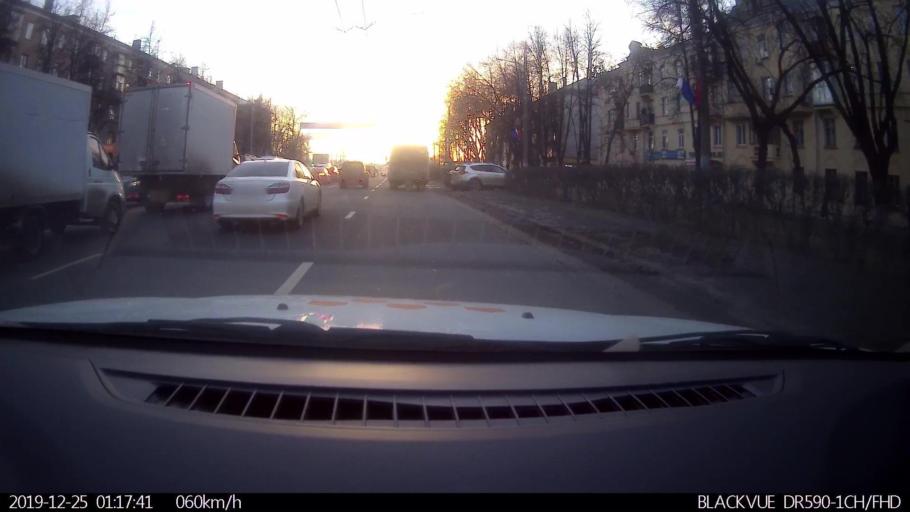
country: RU
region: Nizjnij Novgorod
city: Nizhniy Novgorod
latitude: 56.2642
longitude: 43.9105
